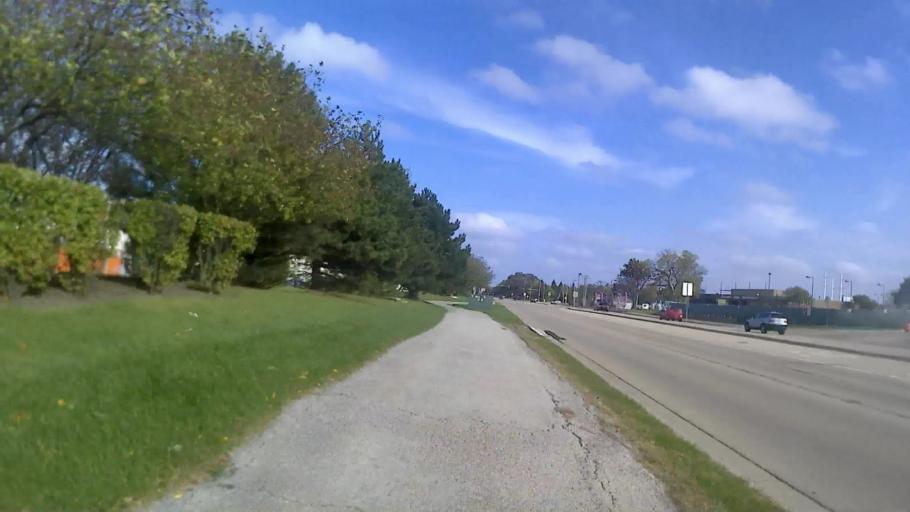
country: US
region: Illinois
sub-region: DuPage County
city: Warrenville
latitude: 41.8077
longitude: -88.1917
